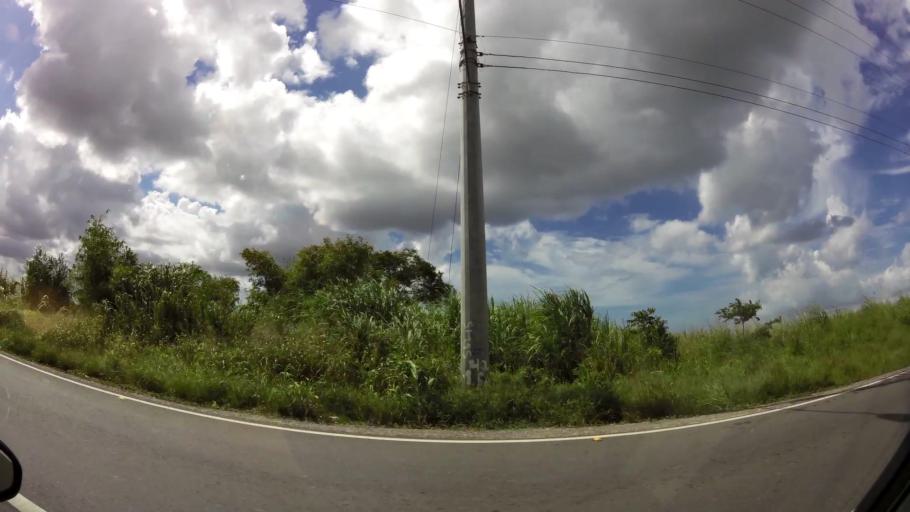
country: TT
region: Penal/Debe
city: Debe
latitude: 10.2365
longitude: -61.4982
